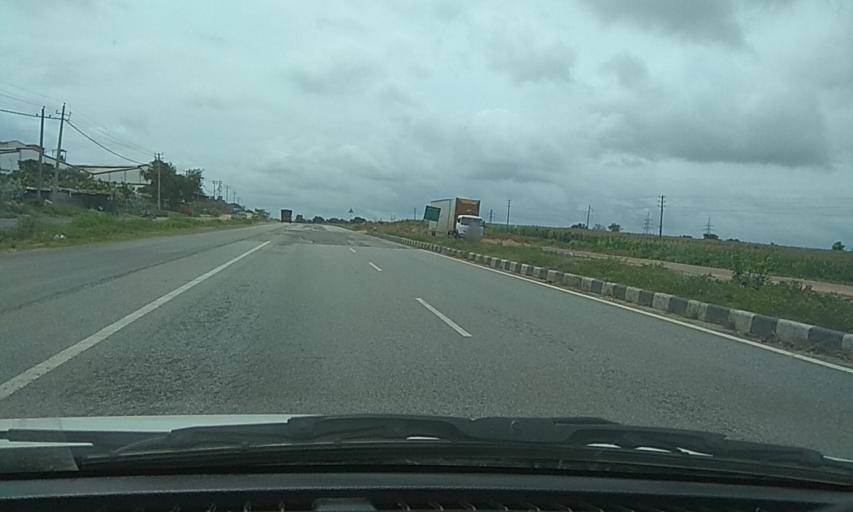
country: IN
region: Karnataka
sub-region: Davanagere
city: Mayakonda
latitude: 14.3374
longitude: 76.2121
